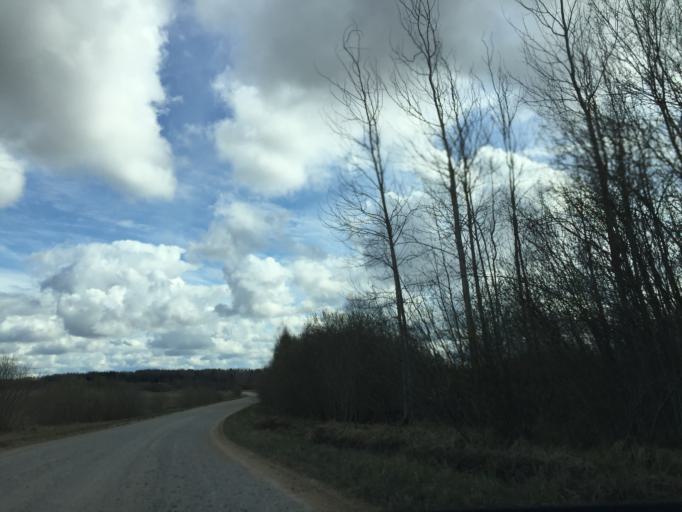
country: LV
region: Limbazu Rajons
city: Limbazi
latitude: 57.6163
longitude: 24.7779
